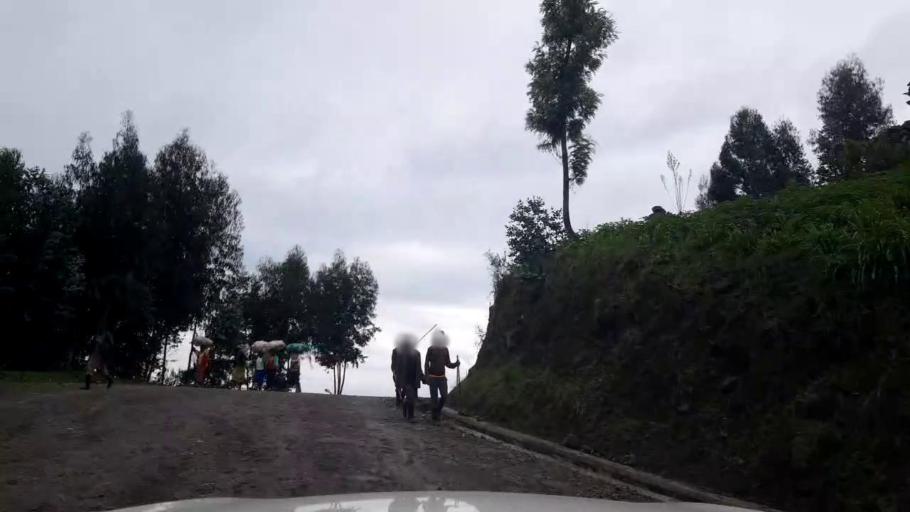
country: RW
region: Northern Province
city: Musanze
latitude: -1.5129
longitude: 29.5347
